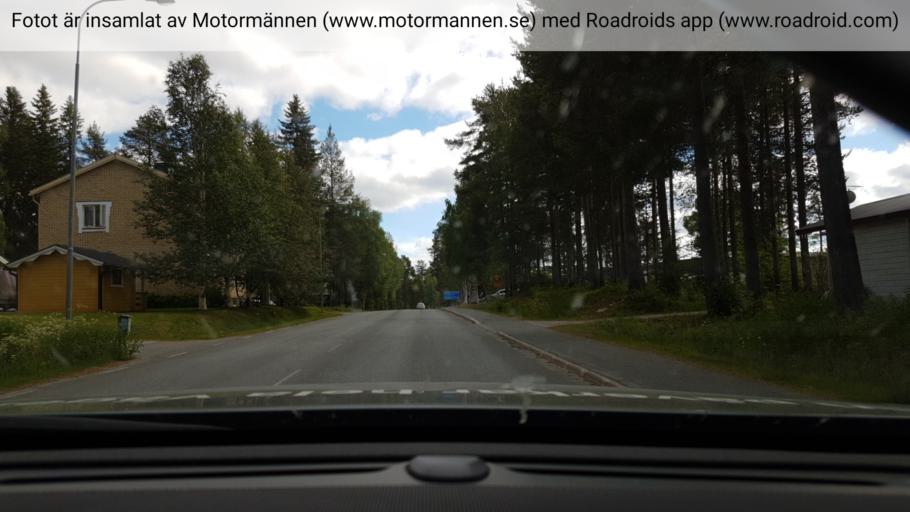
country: SE
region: Vaesterbotten
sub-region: Sorsele Kommun
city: Sorsele
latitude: 65.5392
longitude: 17.5416
